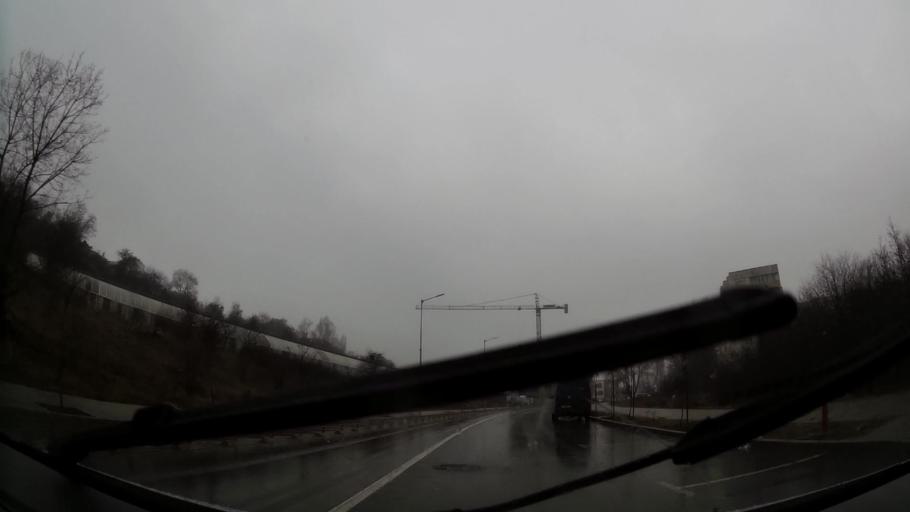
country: BG
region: Sofia-Capital
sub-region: Stolichna Obshtina
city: Sofia
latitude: 42.6523
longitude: 23.3958
